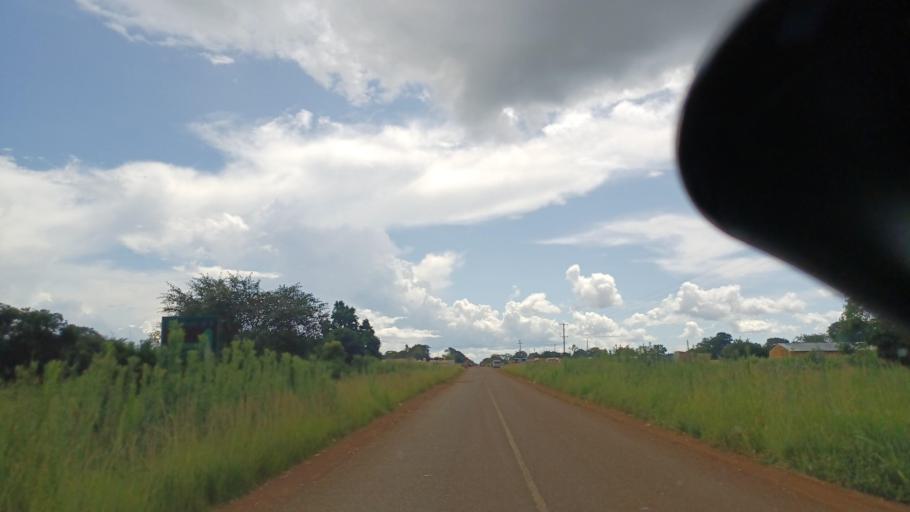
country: ZM
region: North-Western
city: Kasempa
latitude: -13.1040
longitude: 25.8732
